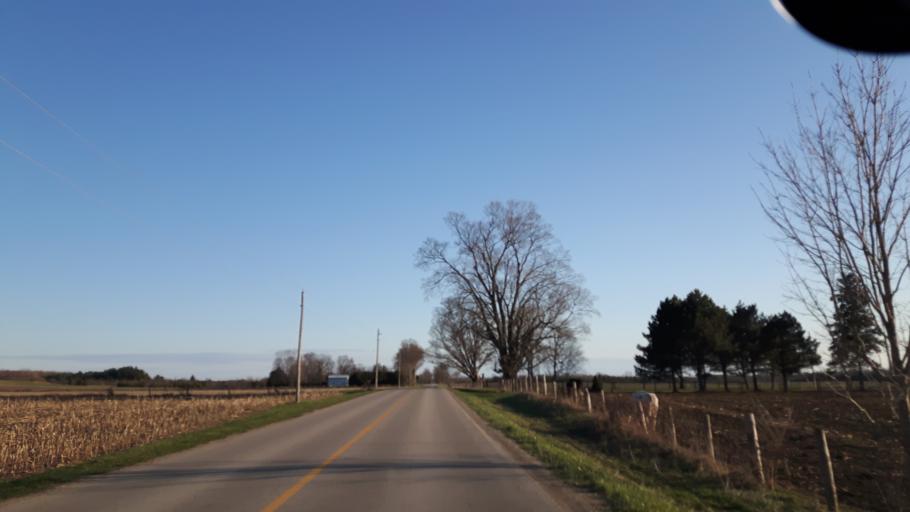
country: CA
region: Ontario
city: Goderich
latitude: 43.6660
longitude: -81.6847
